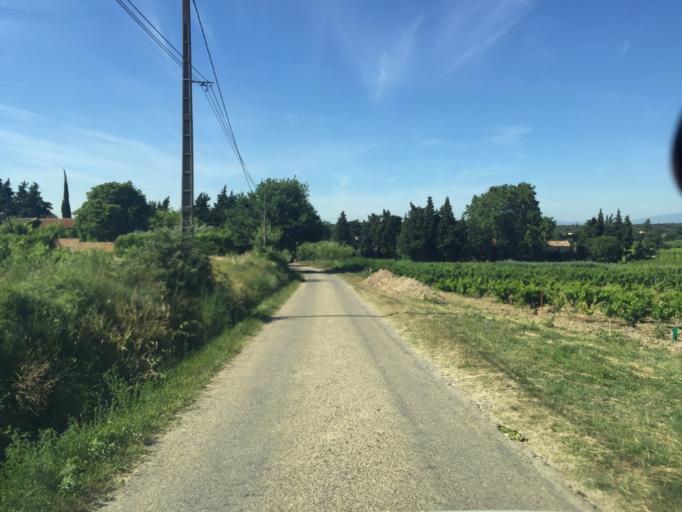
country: FR
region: Provence-Alpes-Cote d'Azur
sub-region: Departement du Vaucluse
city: Orange
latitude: 44.0944
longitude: 4.8056
